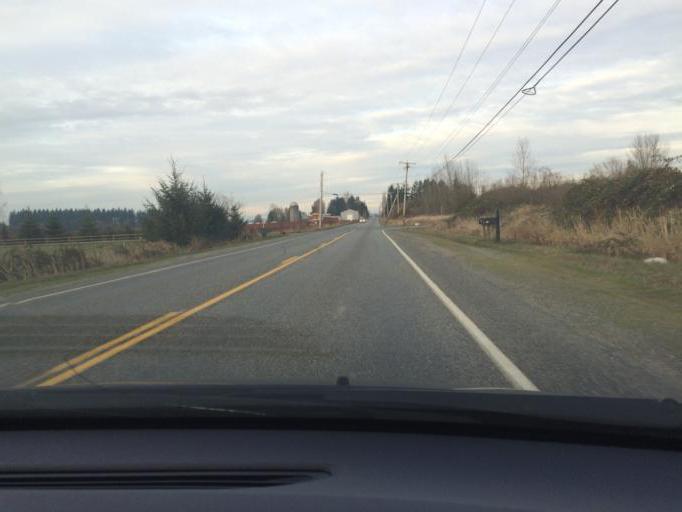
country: US
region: Washington
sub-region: Whatcom County
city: Ferndale
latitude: 48.9198
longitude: -122.5746
